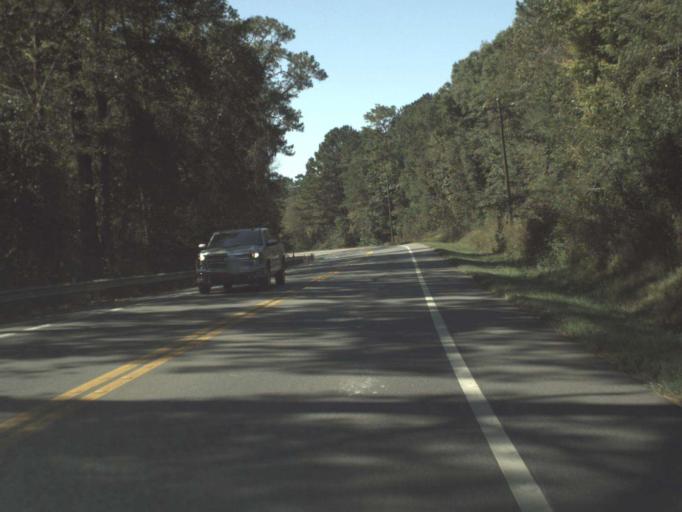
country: US
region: Alabama
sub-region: Covington County
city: Florala
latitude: 30.9654
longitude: -86.4184
